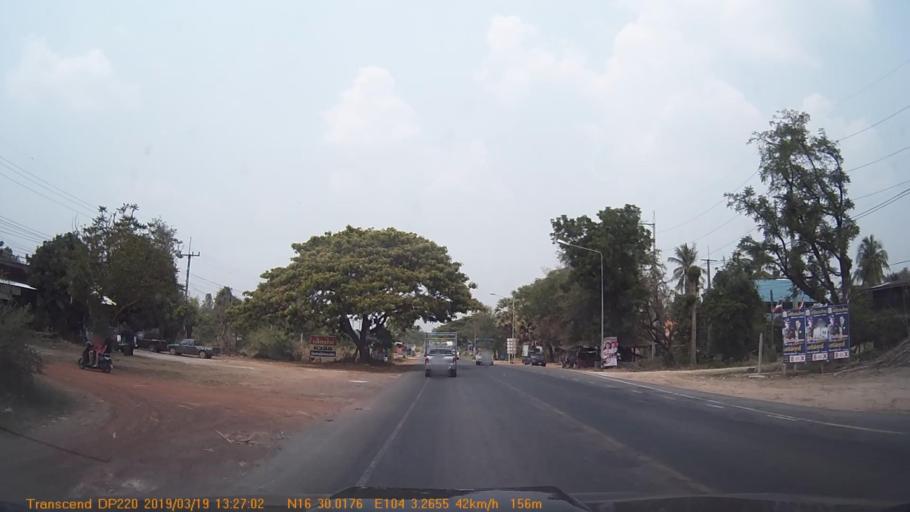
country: TH
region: Kalasin
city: Kuchinarai
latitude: 16.5004
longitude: 104.0545
